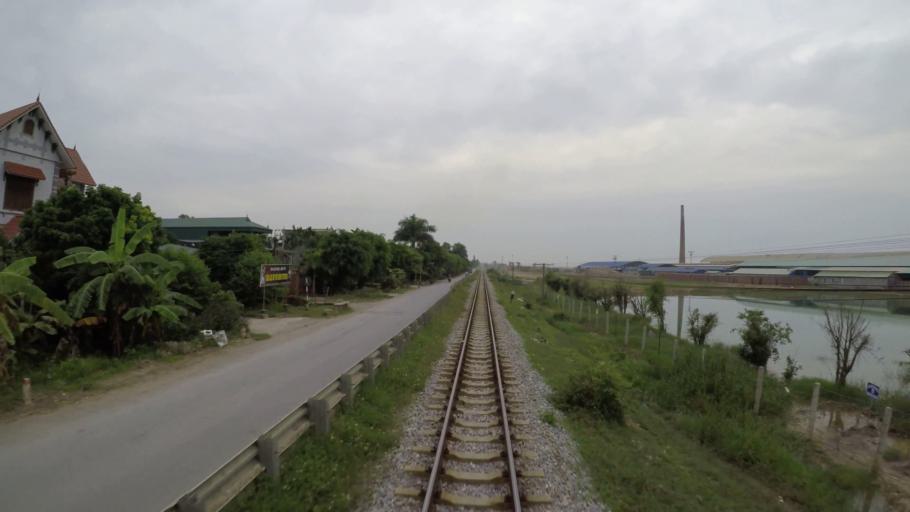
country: VN
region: Hai Duong
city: Ke Sat
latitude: 20.9654
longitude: 106.1173
